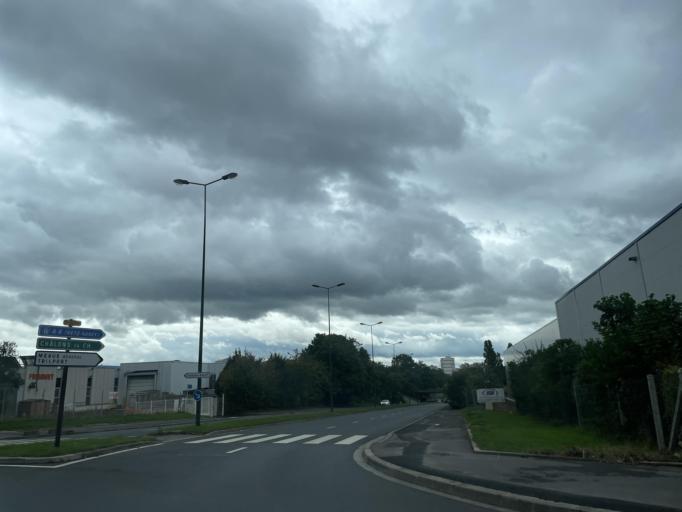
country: FR
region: Ile-de-France
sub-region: Departement de Seine-et-Marne
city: Meaux
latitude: 48.9596
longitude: 2.9112
